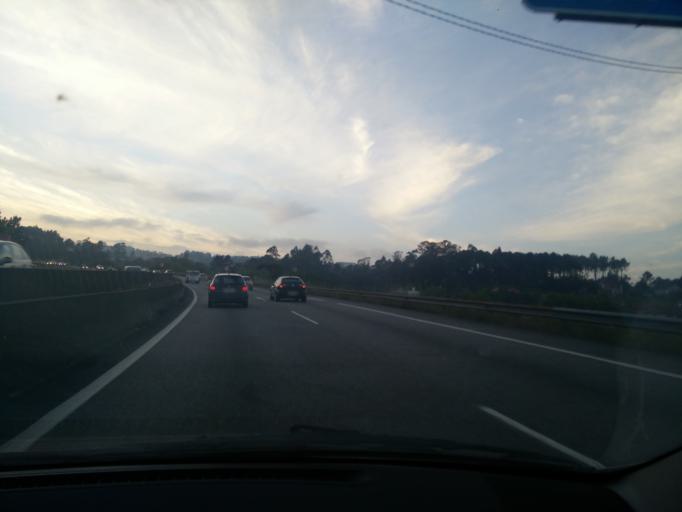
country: ES
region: Galicia
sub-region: Provincia de Pontevedra
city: Porrino
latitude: 42.1911
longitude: -8.6396
